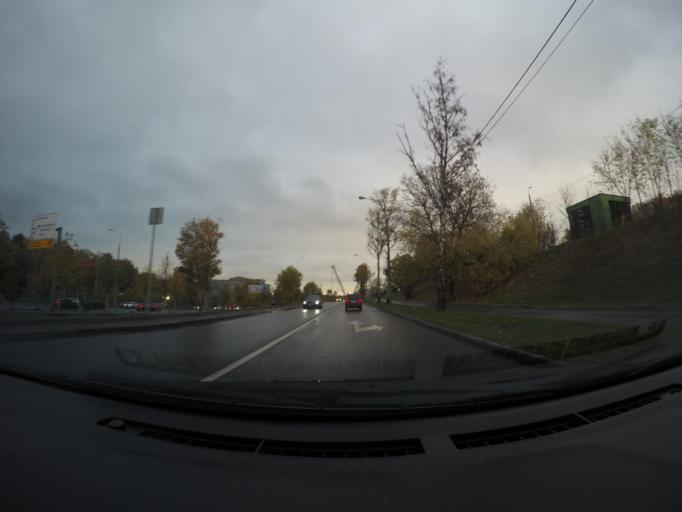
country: RU
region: Moskovskaya
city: Kastanayevo
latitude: 55.7297
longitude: 37.4931
